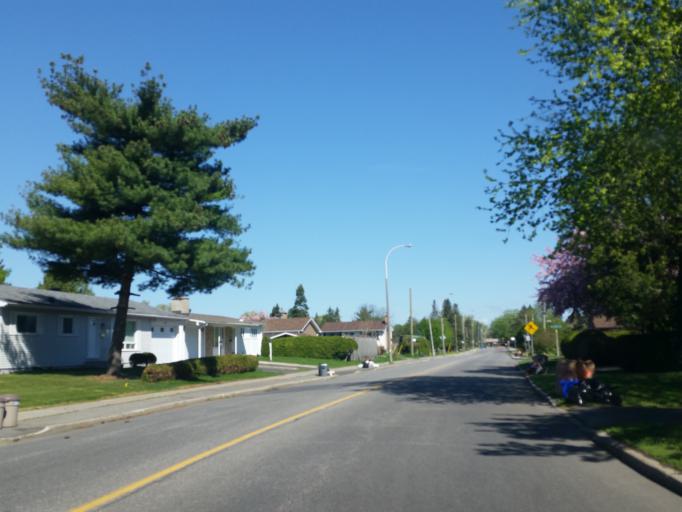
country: CA
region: Ontario
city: Ottawa
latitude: 45.3410
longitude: -75.7444
